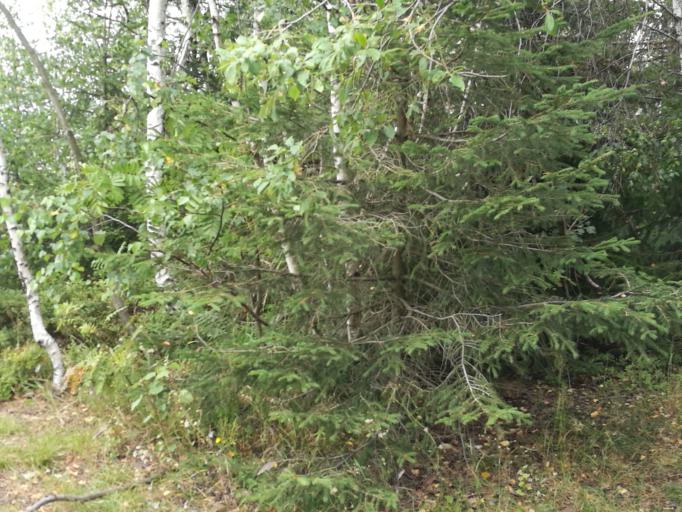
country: CZ
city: Skuhrov nad Belou
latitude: 50.3110
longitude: 16.3273
